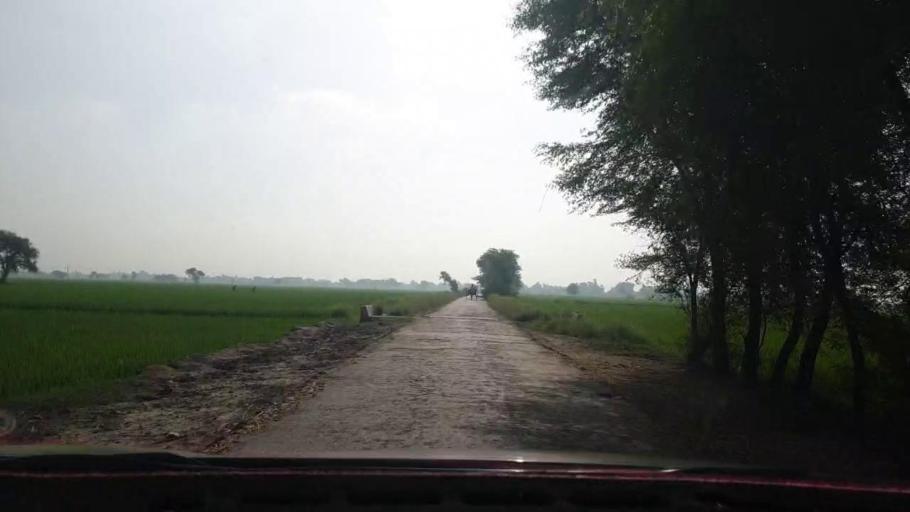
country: PK
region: Sindh
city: Nasirabad
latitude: 27.4561
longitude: 67.9549
